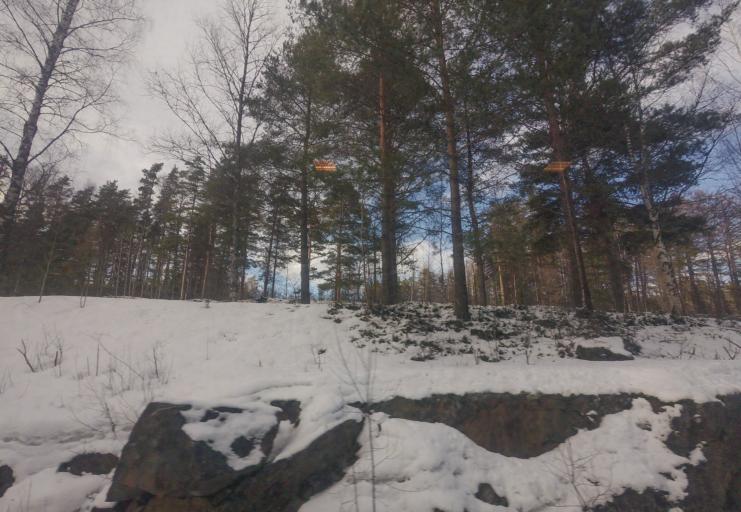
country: FI
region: Southern Savonia
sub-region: Savonlinna
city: Punkaharju
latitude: 61.8047
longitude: 29.3099
